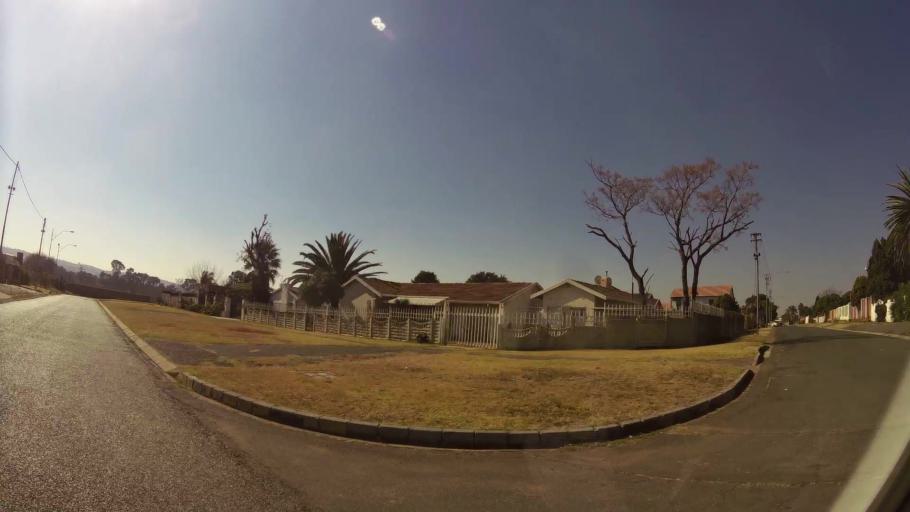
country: ZA
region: Gauteng
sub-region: City of Johannesburg Metropolitan Municipality
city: Johannesburg
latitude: -26.2385
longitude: 28.0741
